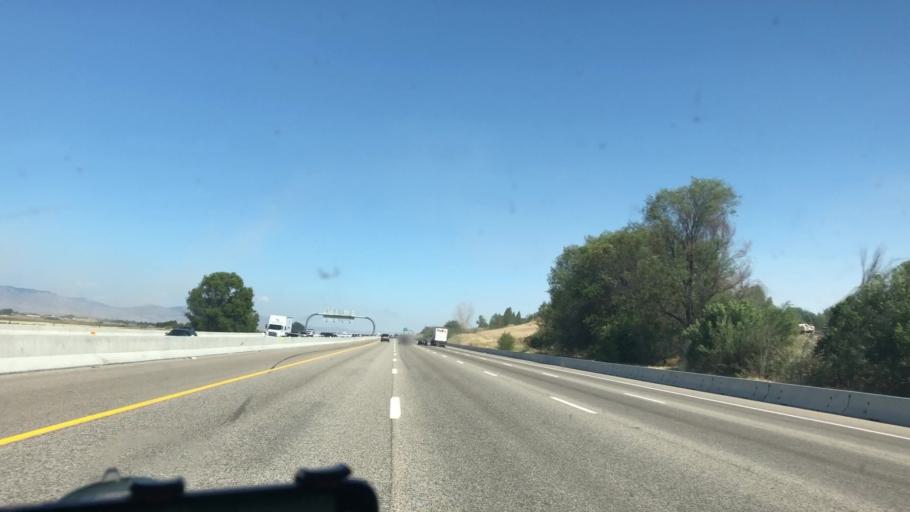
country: US
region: Idaho
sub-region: Ada County
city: Meridian
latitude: 43.5968
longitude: -116.4721
